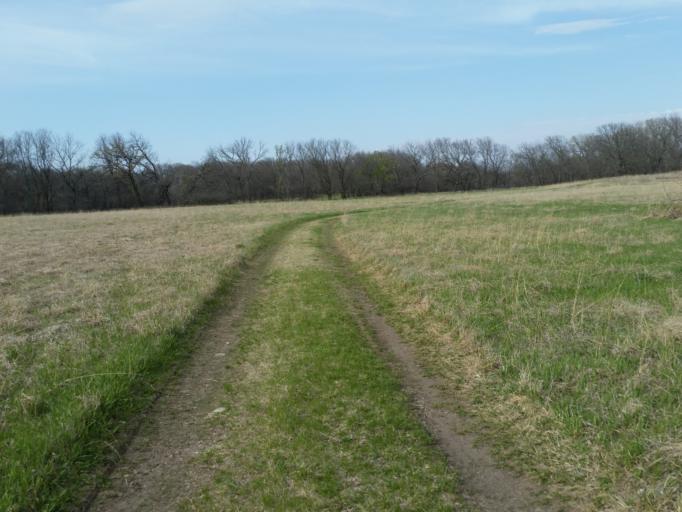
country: US
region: Kansas
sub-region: Chase County
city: Cottonwood Falls
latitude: 38.4369
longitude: -96.5501
